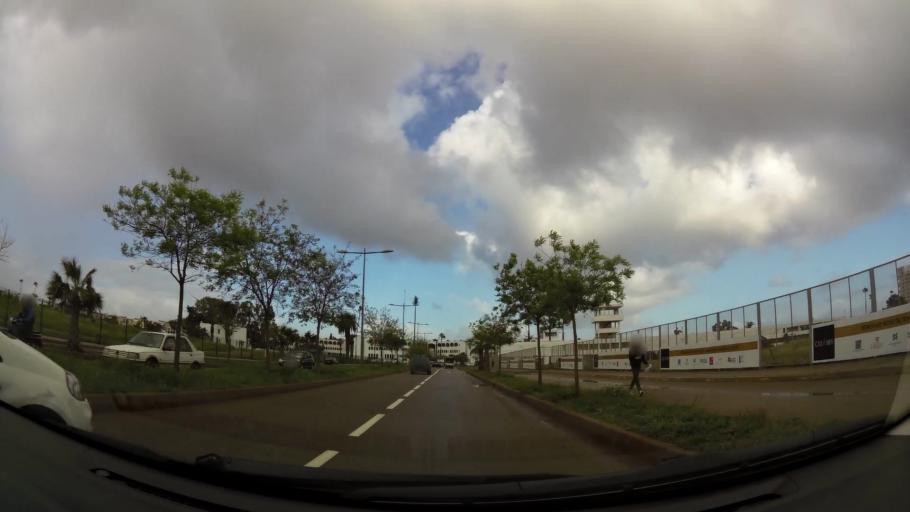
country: MA
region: Grand Casablanca
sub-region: Casablanca
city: Casablanca
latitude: 33.5613
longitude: -7.6621
